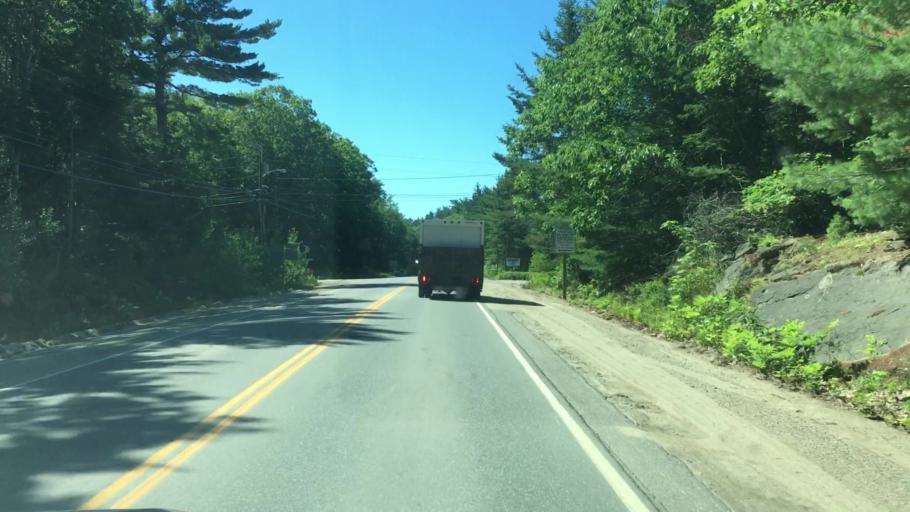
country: US
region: Maine
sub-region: Hancock County
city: Sedgwick
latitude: 44.3805
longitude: -68.5686
